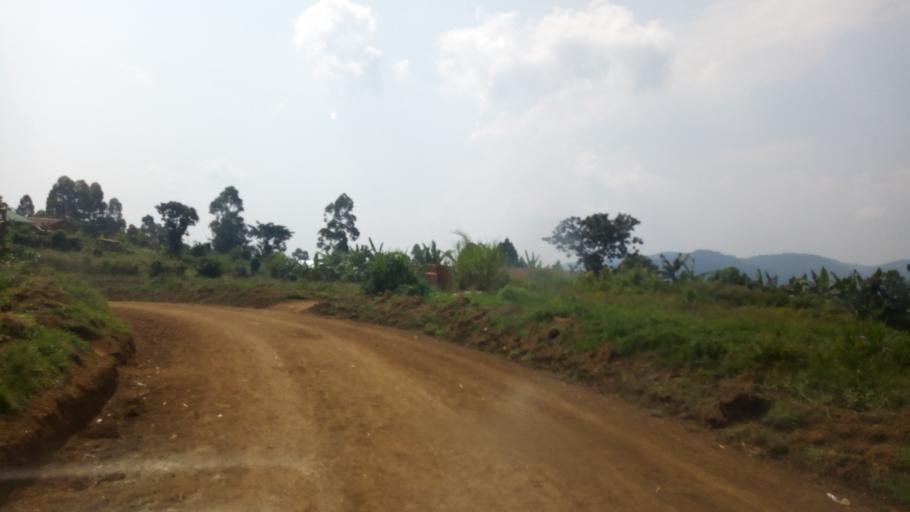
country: UG
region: Western Region
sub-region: Kanungu District
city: Ntungamo
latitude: -1.0215
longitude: 29.5866
